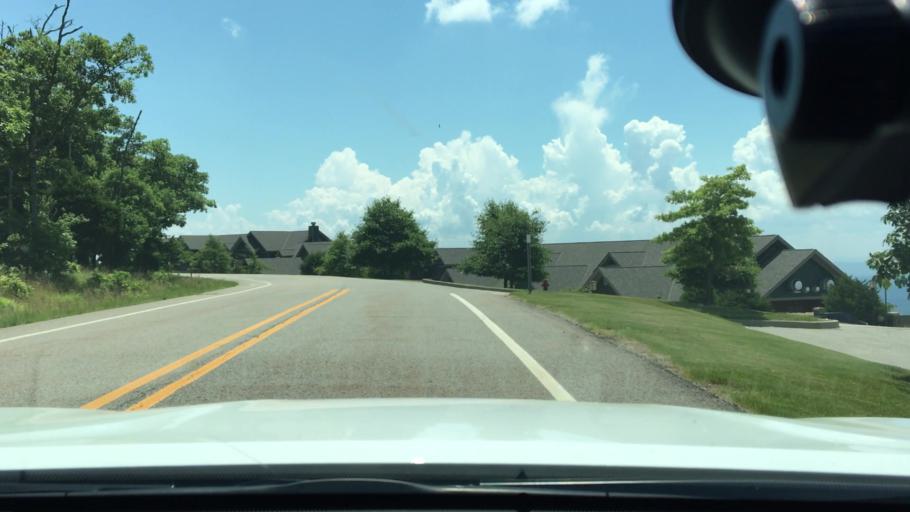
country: US
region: Arkansas
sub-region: Logan County
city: Paris
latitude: 35.1646
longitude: -93.6485
